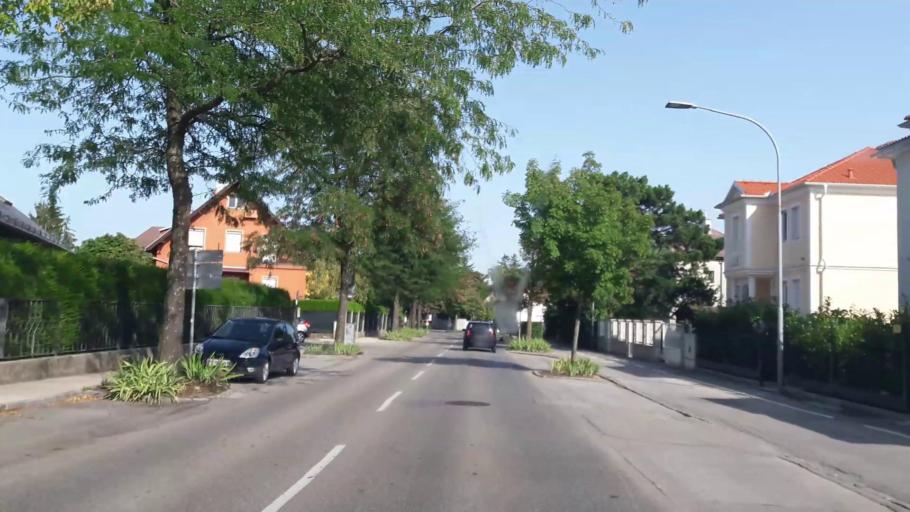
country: AT
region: Lower Austria
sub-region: Politischer Bezirk Modling
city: Perchtoldsdorf
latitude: 48.1239
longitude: 16.2785
